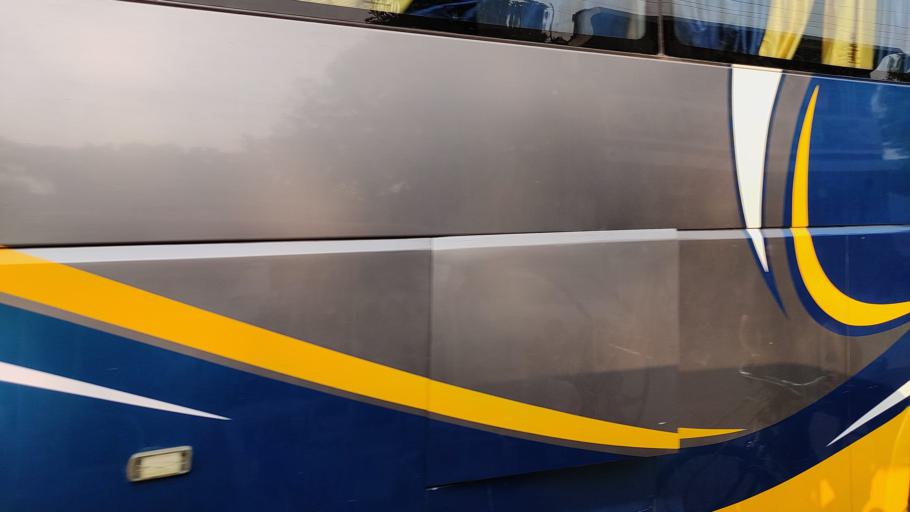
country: IN
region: Uttar Pradesh
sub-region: Mathura
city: Mathura
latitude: 27.5134
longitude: 77.6754
